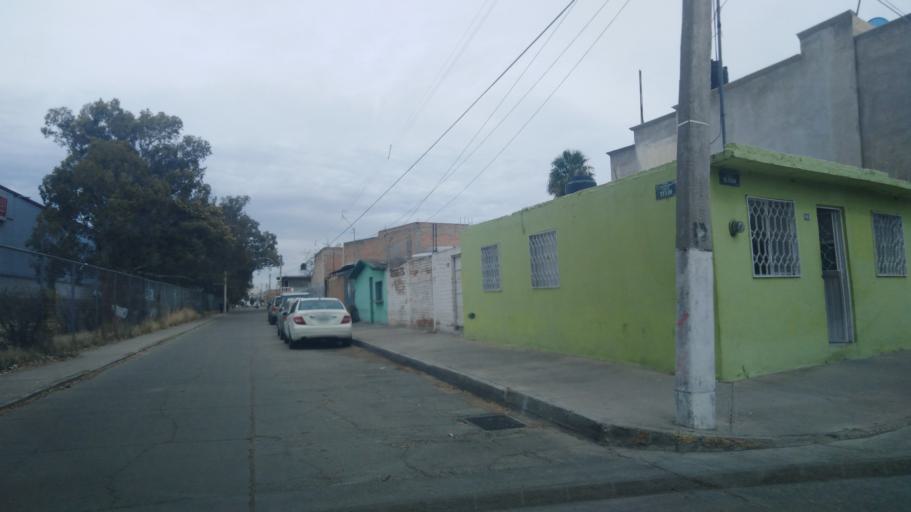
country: MX
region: Durango
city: Victoria de Durango
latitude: 24.0293
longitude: -104.6289
